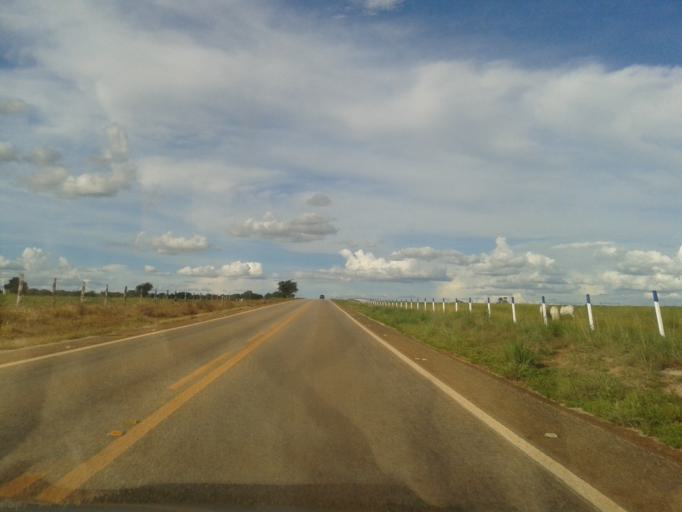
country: BR
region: Goias
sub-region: Mozarlandia
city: Mozarlandia
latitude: -14.3411
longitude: -50.4184
